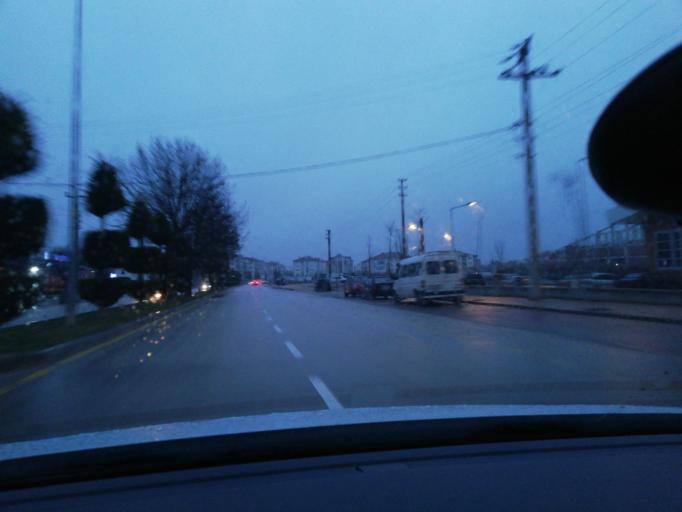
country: TR
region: Bolu
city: Bolu
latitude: 40.7249
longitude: 31.6053
